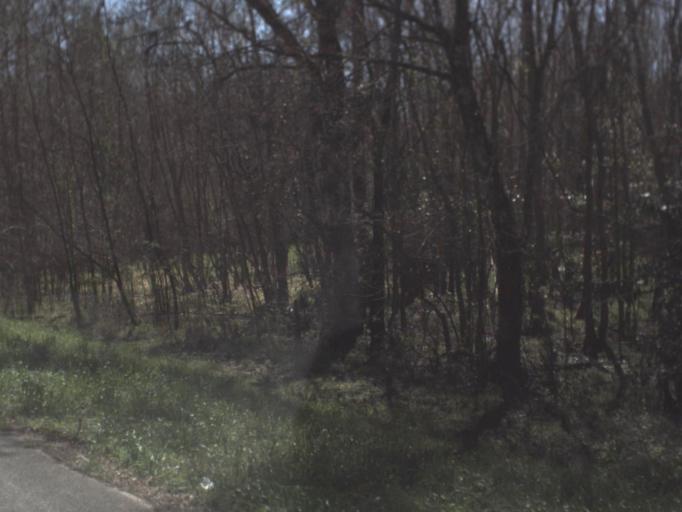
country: US
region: Florida
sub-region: Gadsden County
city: Quincy
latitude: 30.6018
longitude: -84.5813
